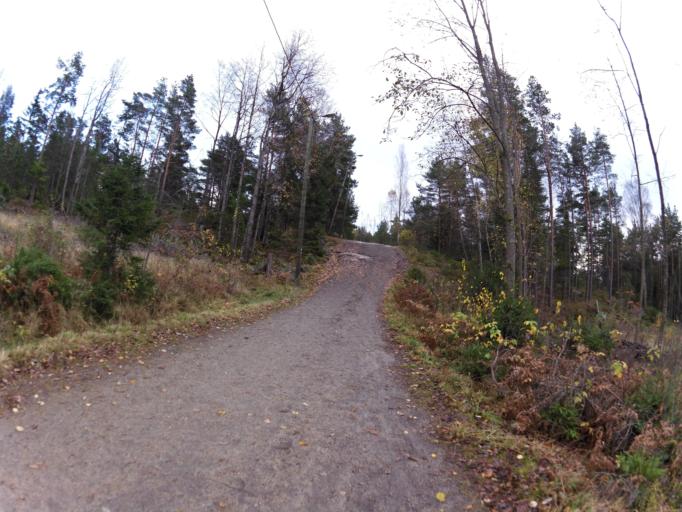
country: NO
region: Ostfold
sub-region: Fredrikstad
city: Fredrikstad
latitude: 59.2407
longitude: 10.9459
